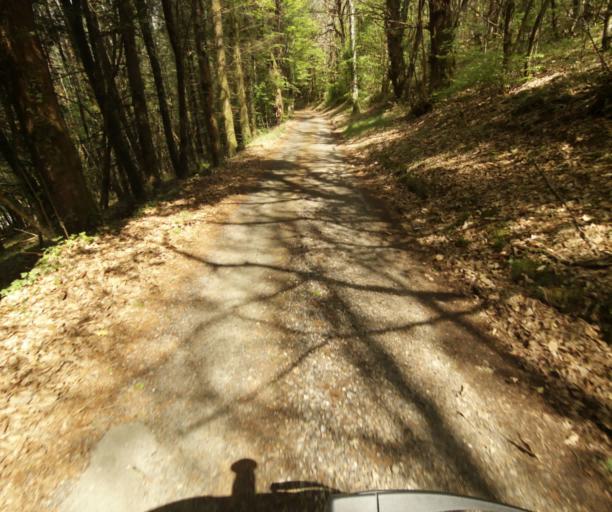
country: FR
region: Limousin
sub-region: Departement de la Correze
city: Naves
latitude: 45.2917
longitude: 1.7756
